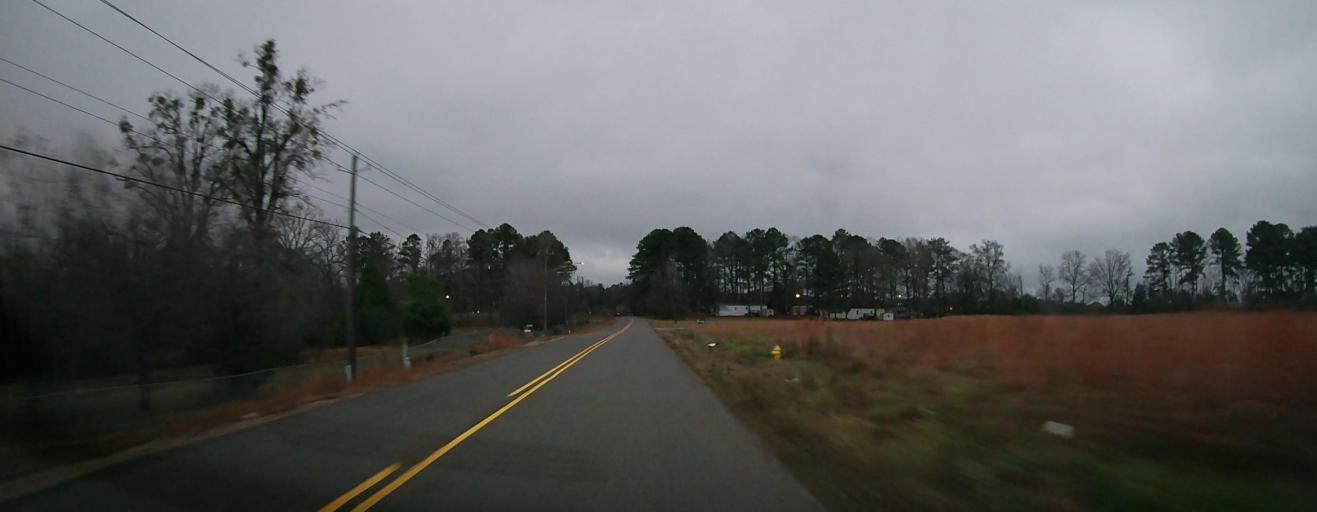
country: US
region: Alabama
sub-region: Tuscaloosa County
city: Vance
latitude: 33.1583
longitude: -87.2299
